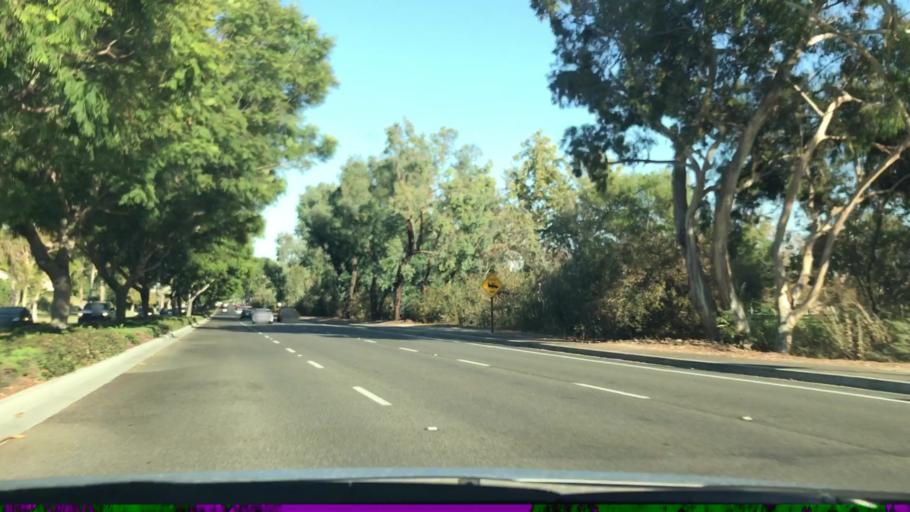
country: US
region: California
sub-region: Orange County
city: Irvine
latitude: 33.6576
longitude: -117.8377
